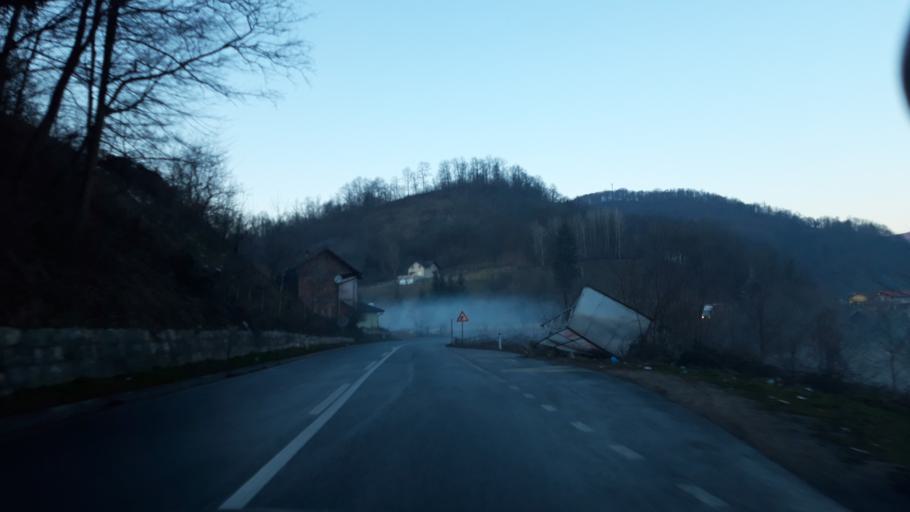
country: RS
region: Central Serbia
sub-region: Macvanski Okrug
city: Mali Zvornik
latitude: 44.3252
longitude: 19.1268
